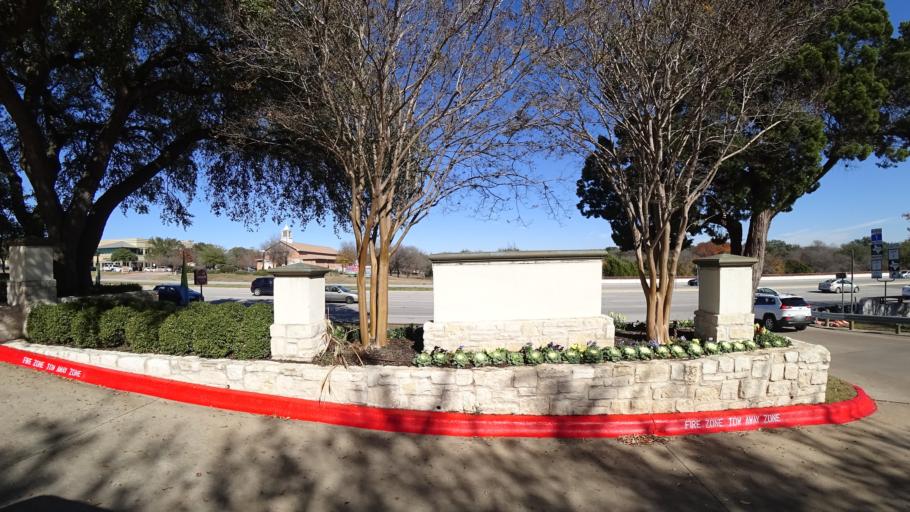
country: US
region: Texas
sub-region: Travis County
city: Wells Branch
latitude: 30.4226
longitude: -97.7094
